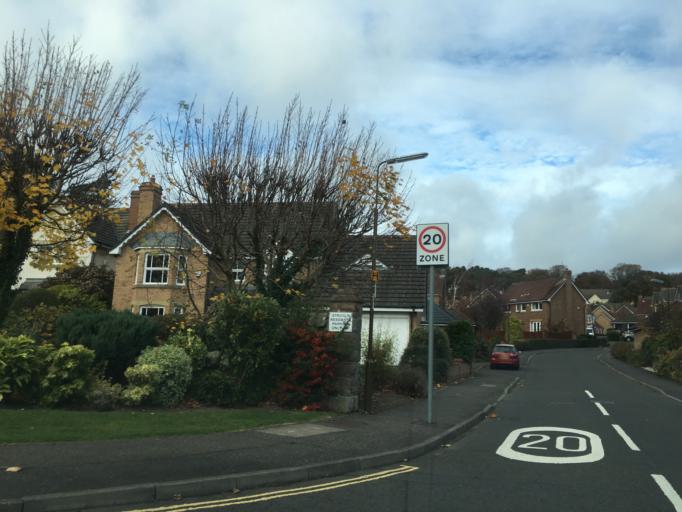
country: GB
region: Scotland
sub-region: Midlothian
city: Loanhead
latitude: 55.8990
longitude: -3.1925
